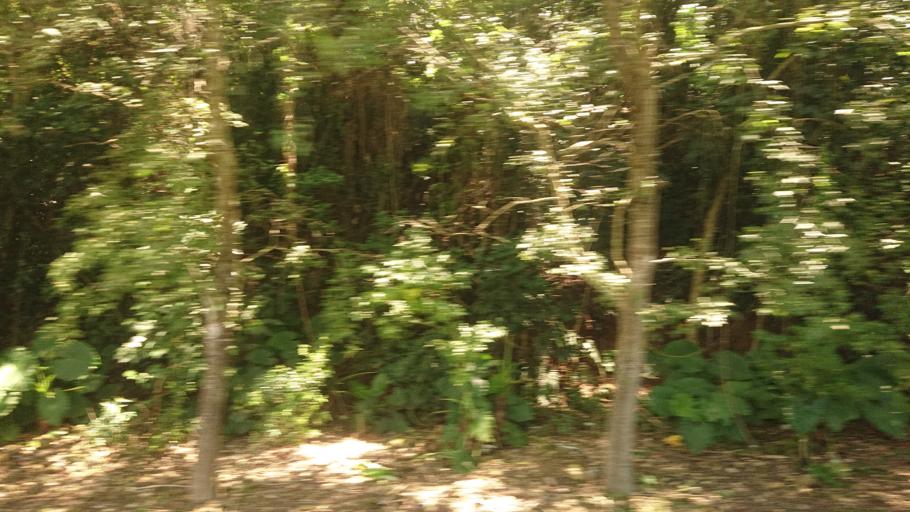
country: TW
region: Taiwan
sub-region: Nantou
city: Puli
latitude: 24.0521
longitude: 120.9345
